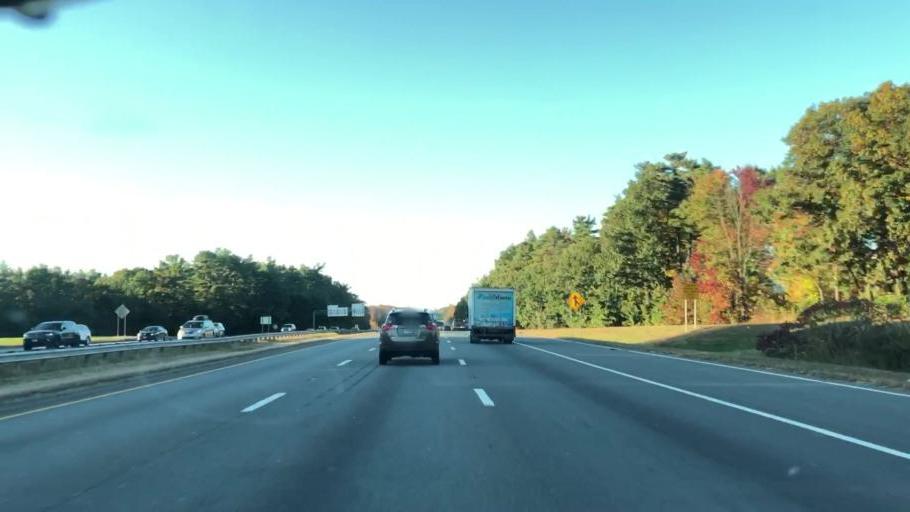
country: US
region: Massachusetts
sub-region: Essex County
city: Andover
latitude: 42.6474
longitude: -71.1865
